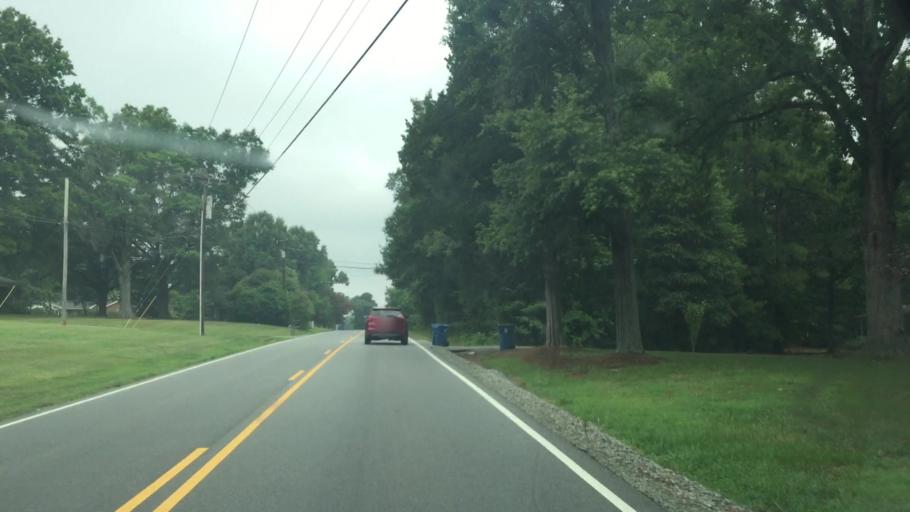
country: US
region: North Carolina
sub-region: Rowan County
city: Enochville
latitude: 35.4699
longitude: -80.7436
